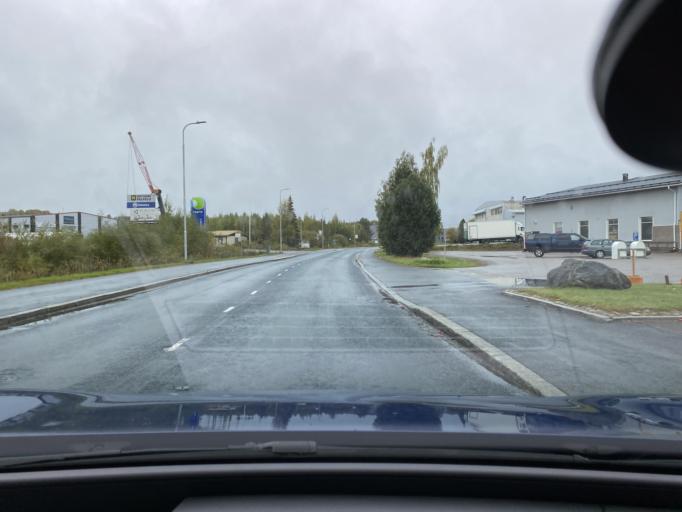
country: FI
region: Pirkanmaa
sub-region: Tampere
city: Tampere
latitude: 61.4565
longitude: 23.7348
